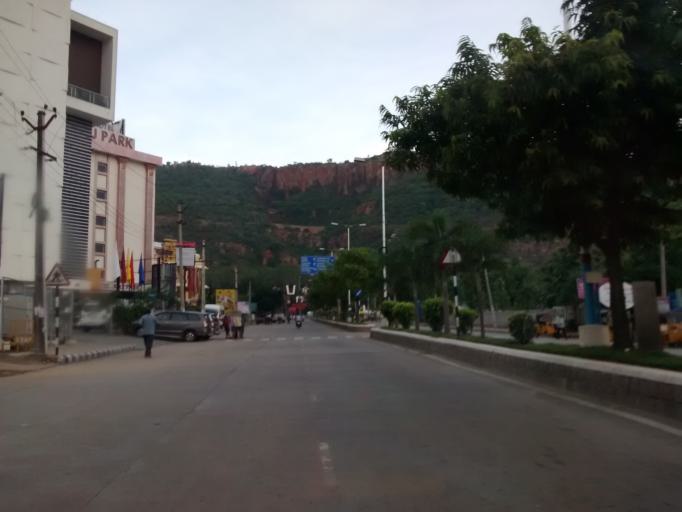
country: IN
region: Andhra Pradesh
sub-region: Chittoor
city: Akkarampalle
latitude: 13.6524
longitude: 79.4217
